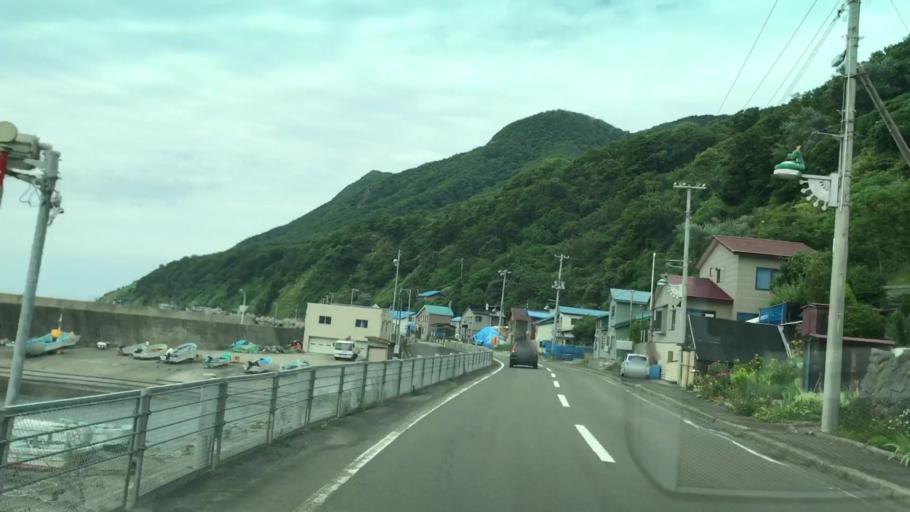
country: JP
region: Hokkaido
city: Iwanai
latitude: 43.1565
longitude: 140.4044
